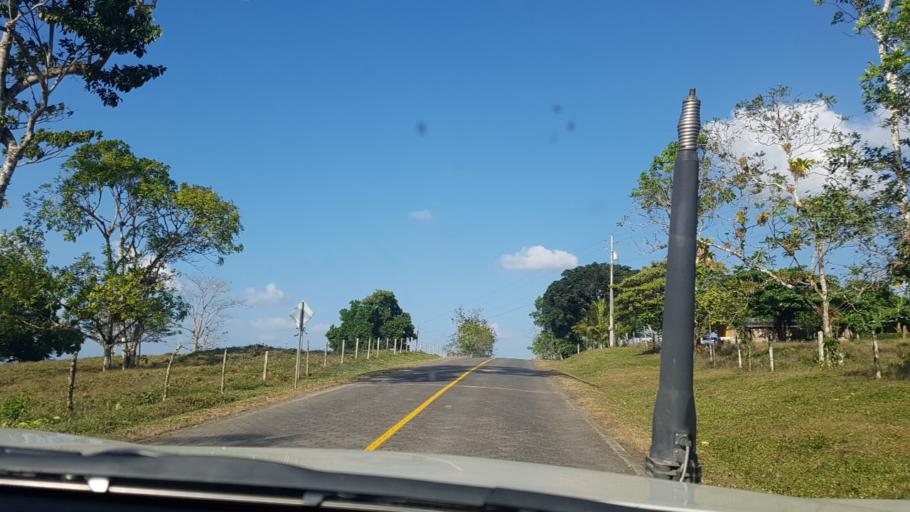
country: NI
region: Atlantico Sur
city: Nueva Guinea
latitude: 11.6926
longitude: -84.4152
